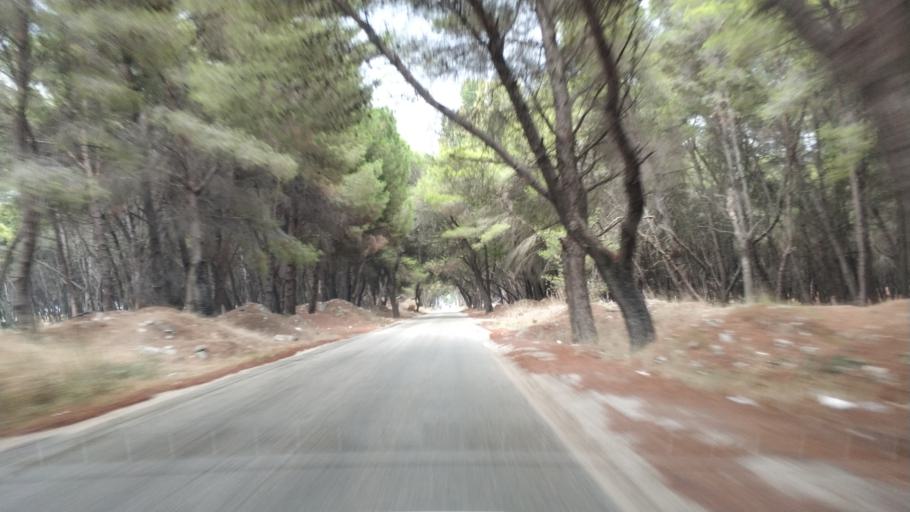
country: AL
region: Vlore
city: Vlore
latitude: 40.4694
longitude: 19.4599
